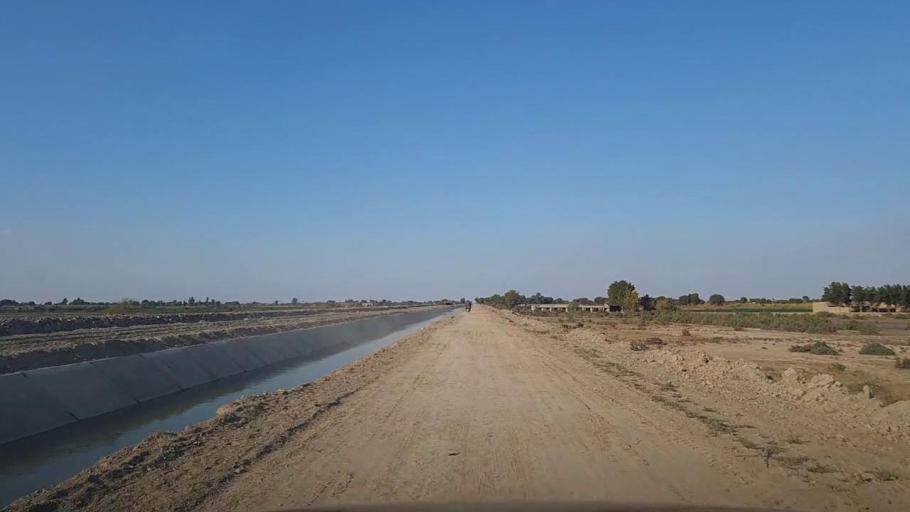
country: PK
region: Sindh
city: Jhol
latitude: 25.8887
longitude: 69.0379
